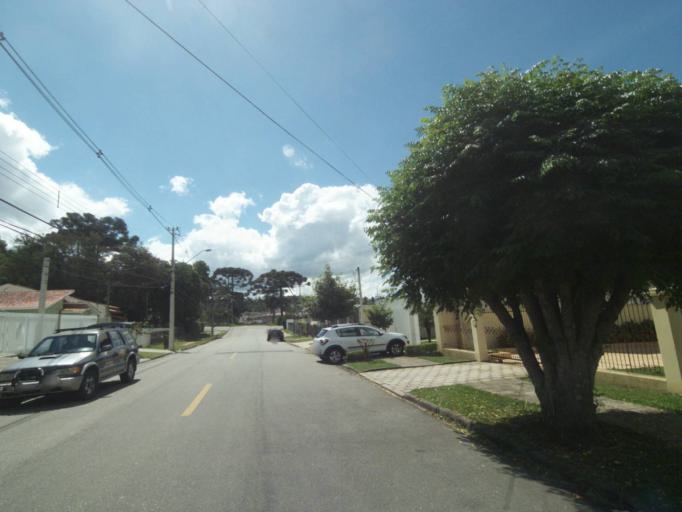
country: BR
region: Parana
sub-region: Curitiba
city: Curitiba
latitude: -25.4349
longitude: -49.3341
